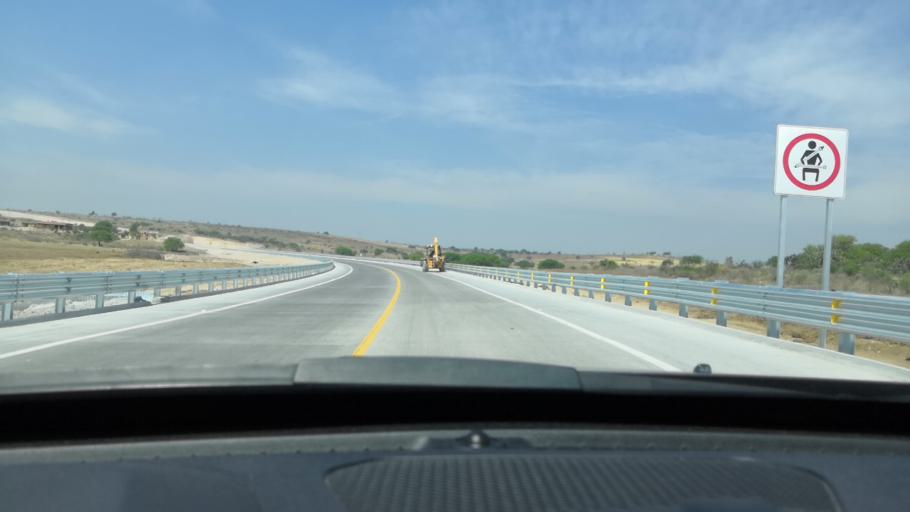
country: MX
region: Guanajuato
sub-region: Purisima del Rincon
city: Potrerillos (Guanajal)
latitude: 21.0863
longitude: -101.8495
